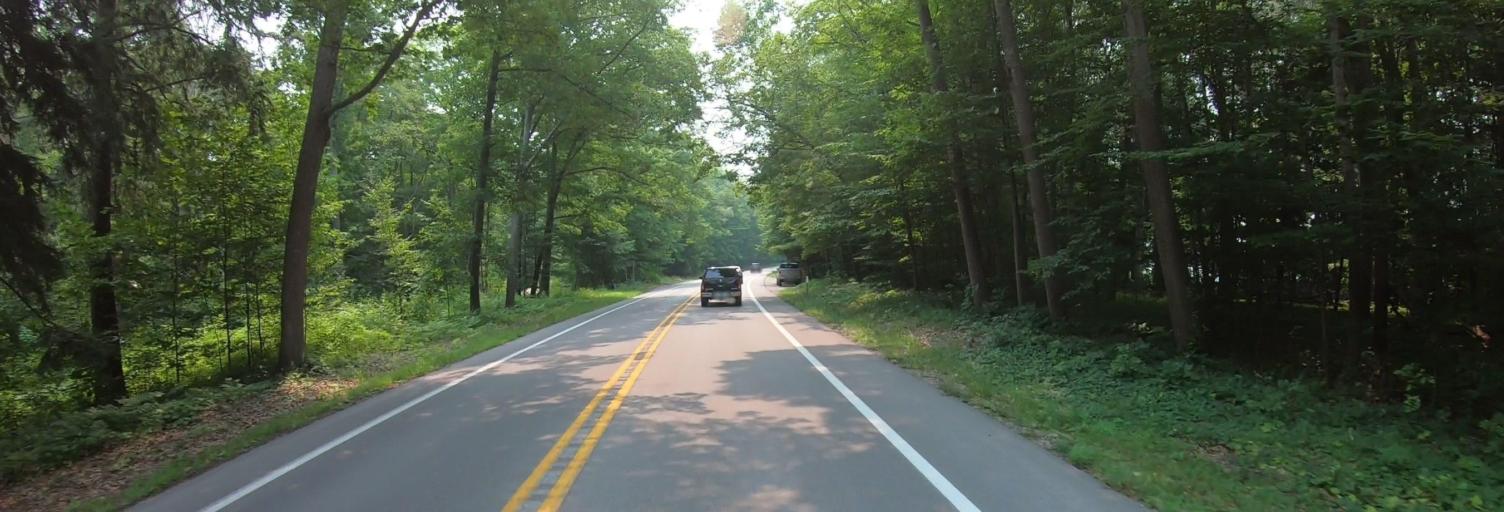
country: US
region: Michigan
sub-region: Leelanau County
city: Leland
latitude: 44.9298
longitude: -85.8853
